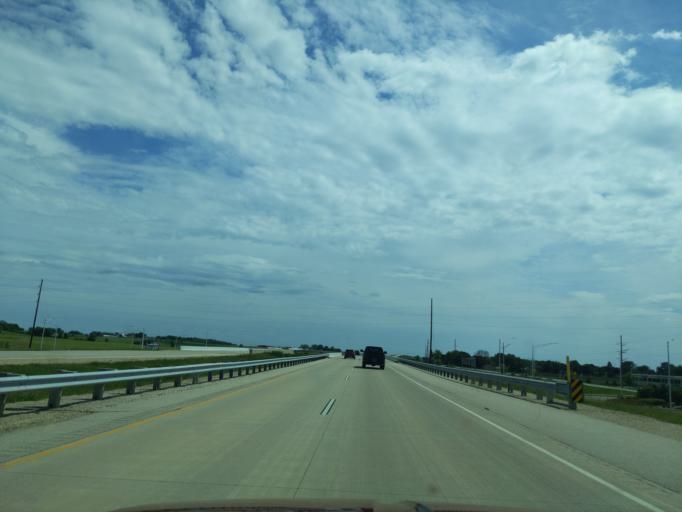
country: US
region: Wisconsin
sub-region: Dane County
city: De Forest
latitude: 43.2540
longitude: -89.3245
